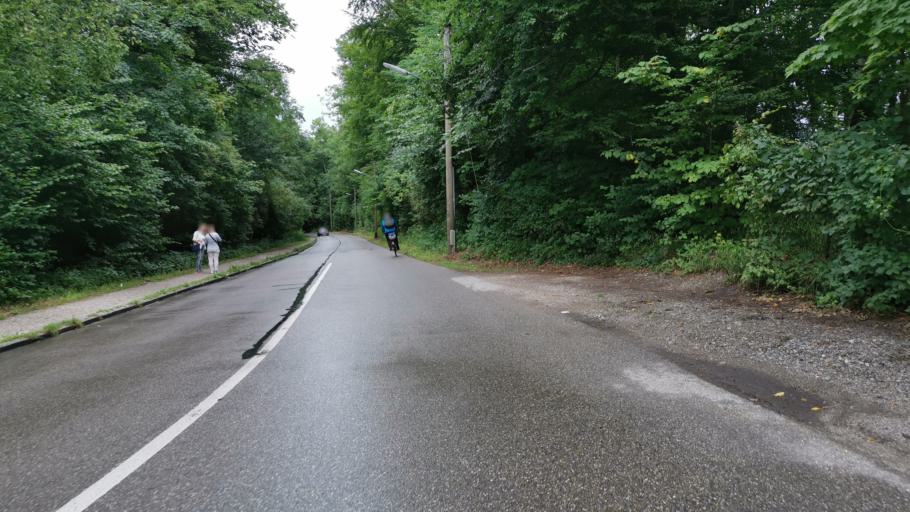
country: DE
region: Bavaria
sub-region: Upper Bavaria
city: Pullach im Isartal
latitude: 48.0753
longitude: 11.5363
